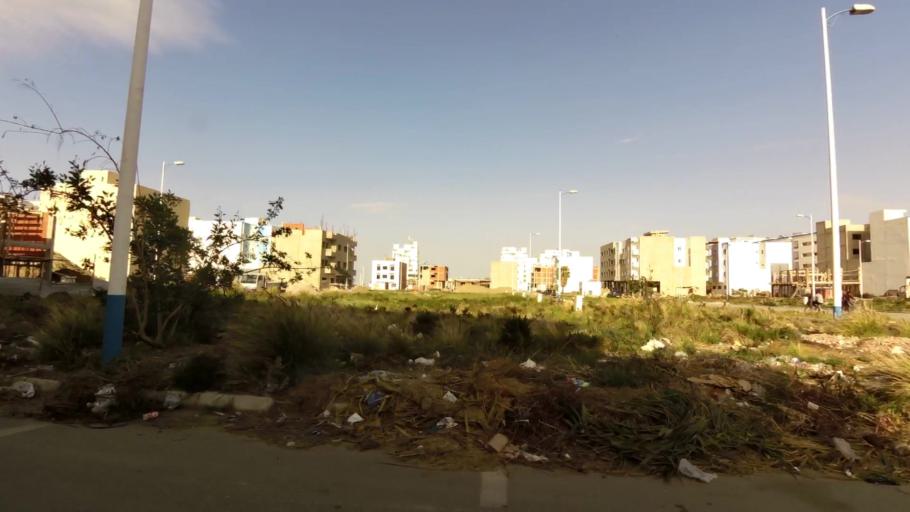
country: MA
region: Tanger-Tetouan
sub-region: Tetouan
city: Martil
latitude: 35.6298
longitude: -5.2783
